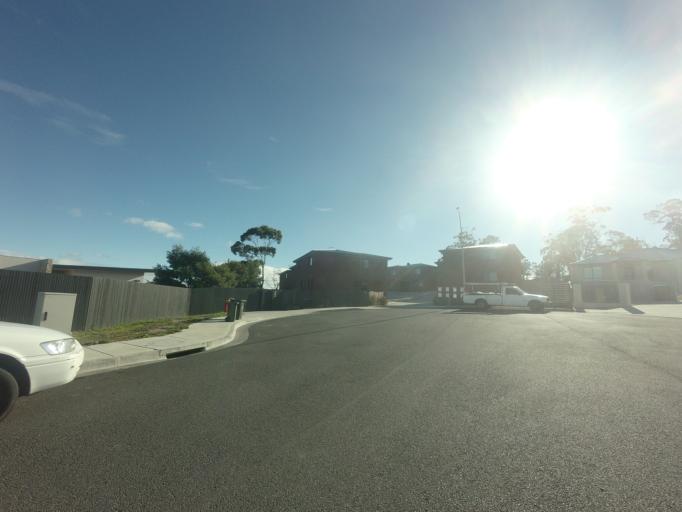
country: AU
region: Tasmania
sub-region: Clarence
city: Rokeby
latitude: -42.8975
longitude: 147.4515
